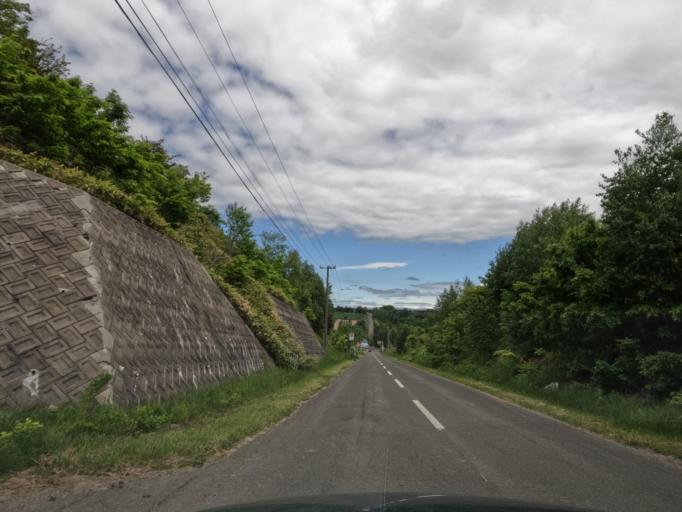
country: JP
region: Hokkaido
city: Shimo-furano
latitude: 43.5307
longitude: 142.4395
